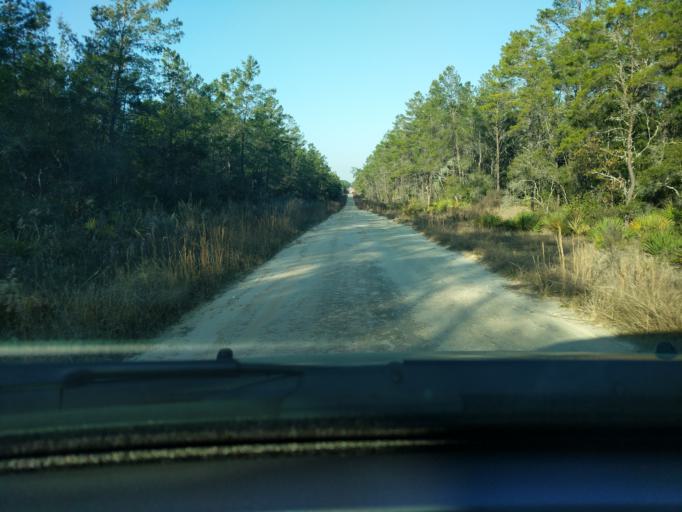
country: US
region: Florida
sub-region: Lake County
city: Astor
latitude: 29.2260
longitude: -81.7623
